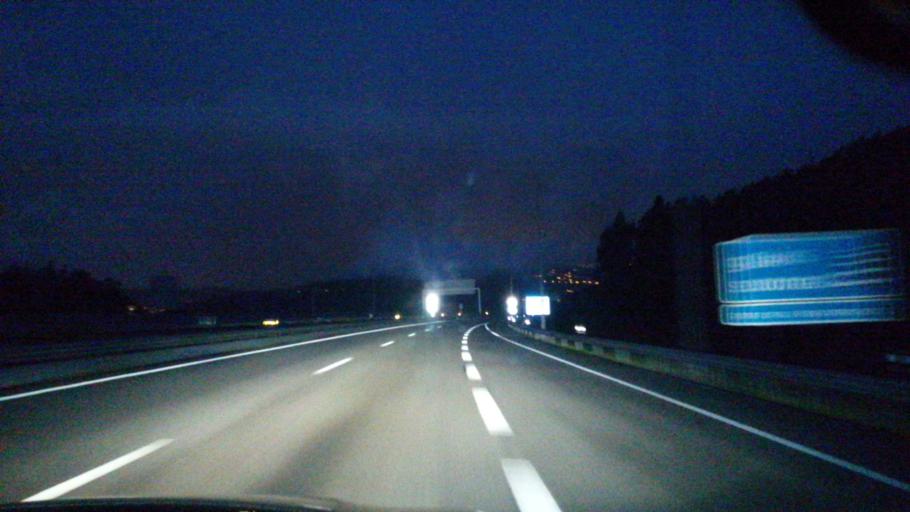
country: PT
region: Porto
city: Barrosas
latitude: 41.3522
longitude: -8.2677
